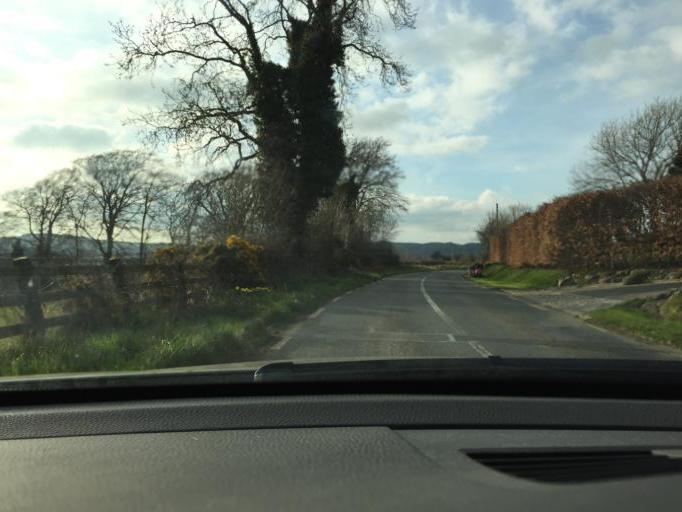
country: IE
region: Leinster
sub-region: Wicklow
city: Blessington
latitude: 53.1628
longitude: -6.5214
